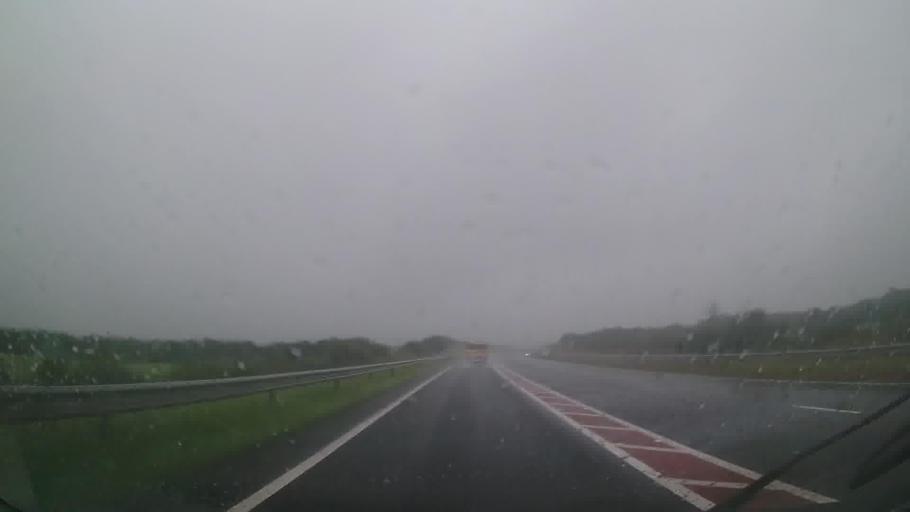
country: GB
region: Wales
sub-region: Carmarthenshire
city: Whitland
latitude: 51.7814
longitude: -4.6053
